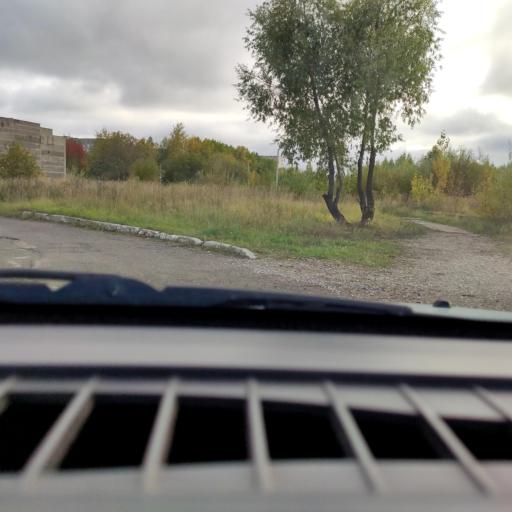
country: RU
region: Perm
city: Froly
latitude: 57.9529
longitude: 56.2699
